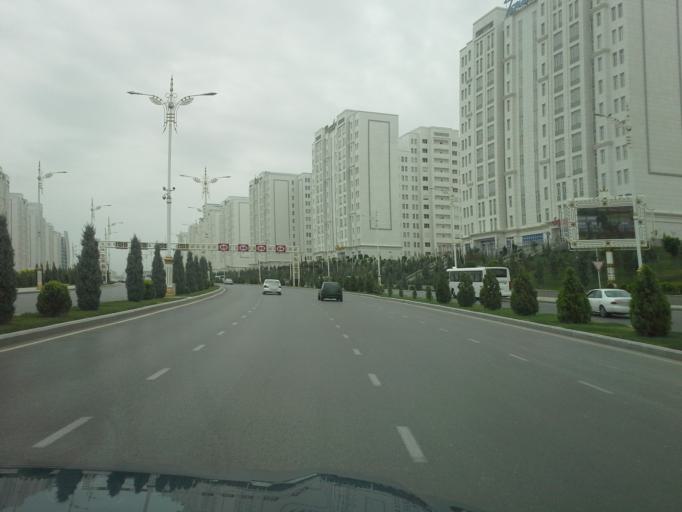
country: TM
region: Ahal
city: Ashgabat
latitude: 37.9386
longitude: 58.3645
